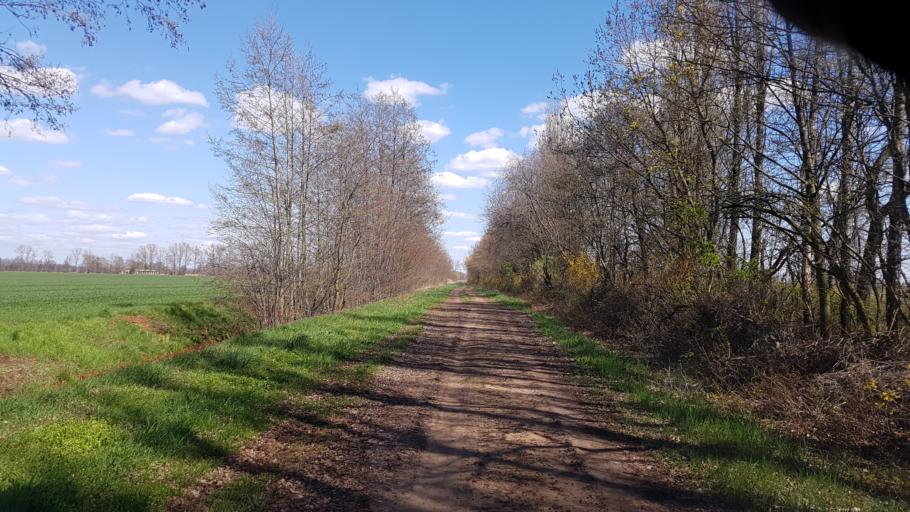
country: DE
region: Brandenburg
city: Bad Liebenwerda
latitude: 51.4953
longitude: 13.3416
